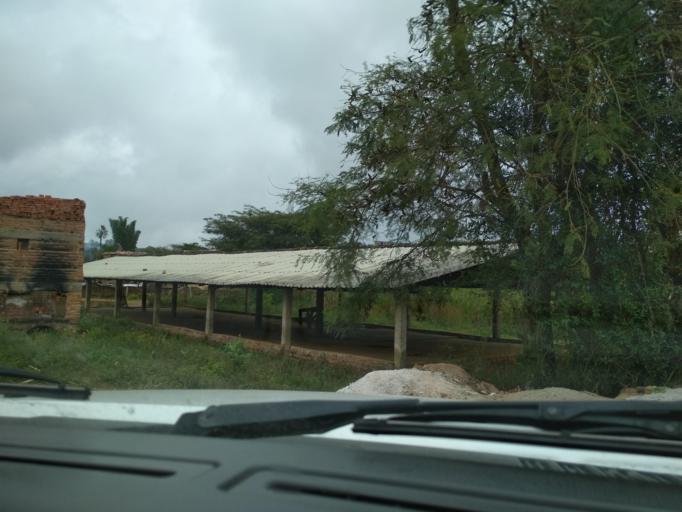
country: MX
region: Veracruz
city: El Castillo
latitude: 19.5459
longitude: -96.8506
